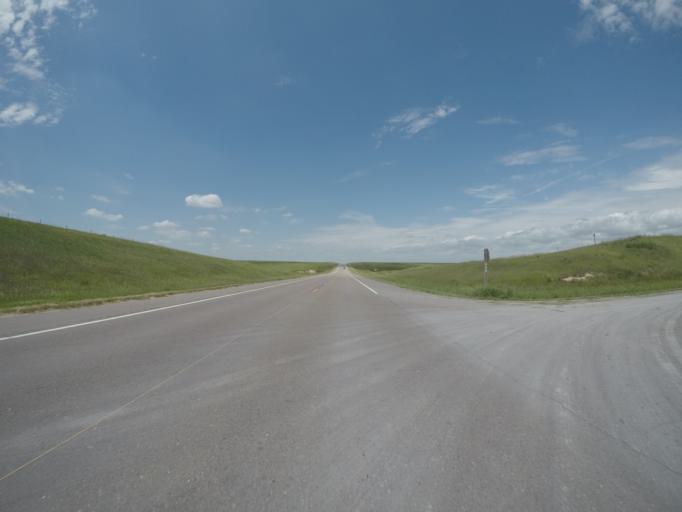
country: US
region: Kansas
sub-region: Graham County
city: Hill City
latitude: 39.3794
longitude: -99.7147
